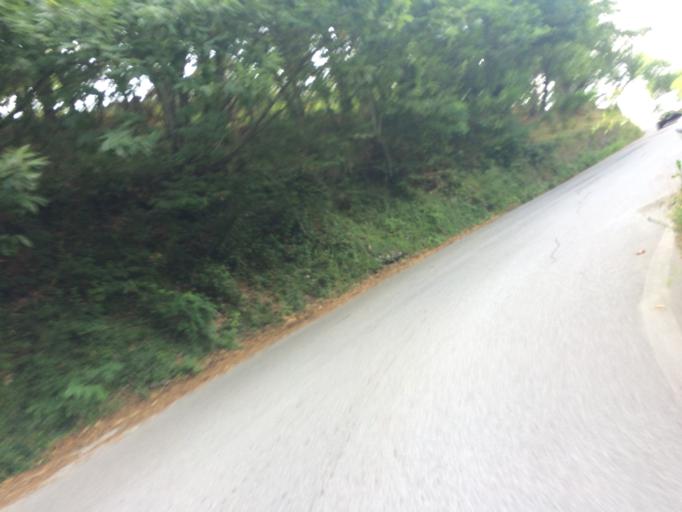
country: IT
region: Liguria
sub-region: Provincia di Savona
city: San Giovanni
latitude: 44.4007
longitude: 8.4941
